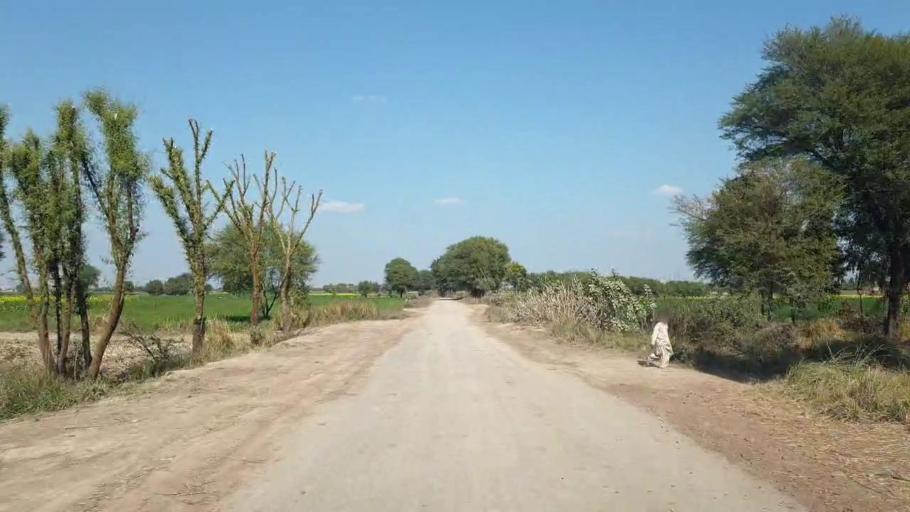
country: PK
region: Sindh
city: Shahpur Chakar
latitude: 26.0792
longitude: 68.5847
